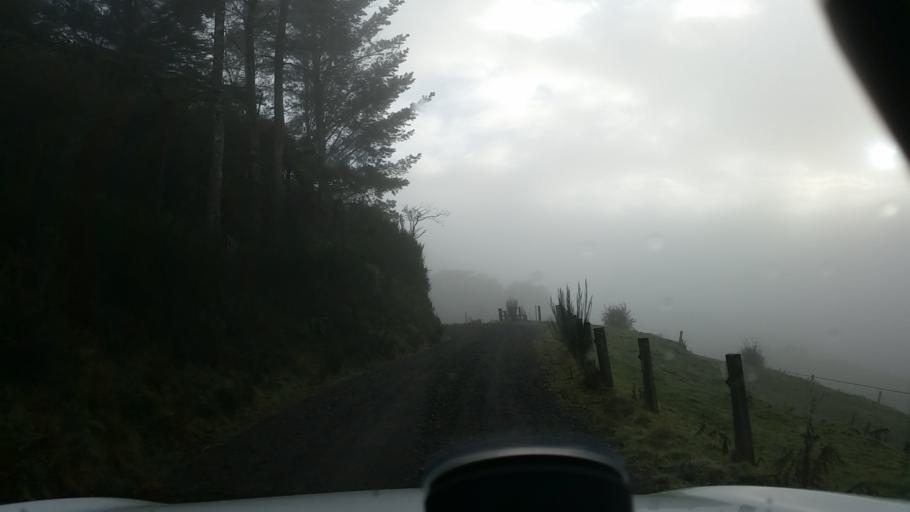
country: NZ
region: Taranaki
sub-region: South Taranaki District
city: Eltham
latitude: -39.4141
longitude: 174.4295
